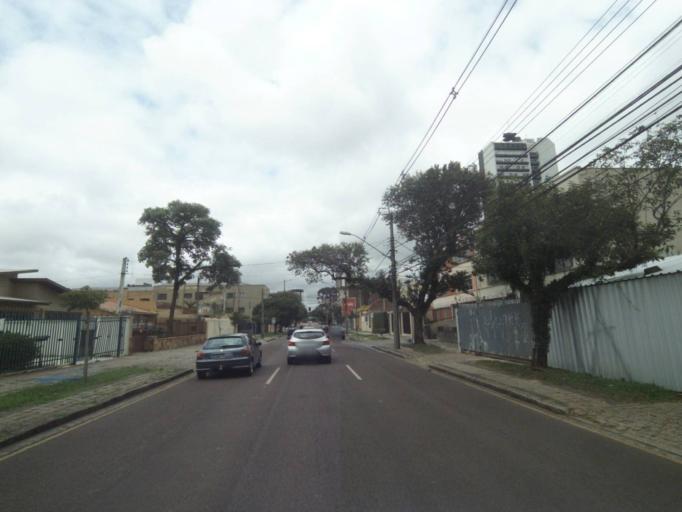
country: BR
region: Parana
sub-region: Curitiba
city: Curitiba
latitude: -25.4286
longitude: -49.2553
